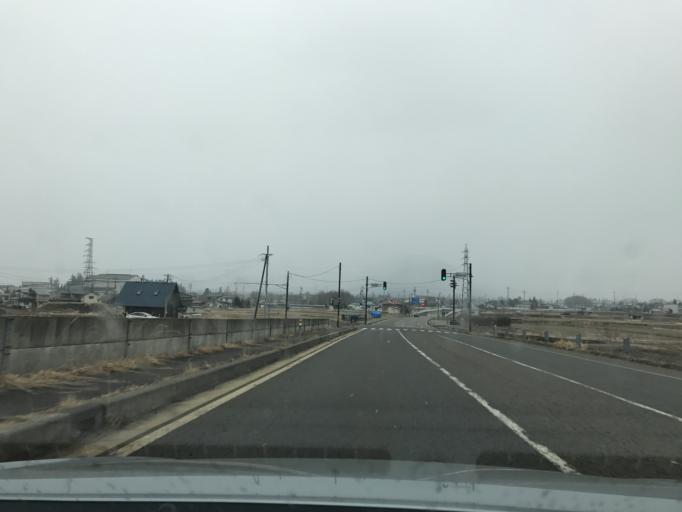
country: JP
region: Nagano
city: Omachi
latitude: 36.5232
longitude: 137.8598
